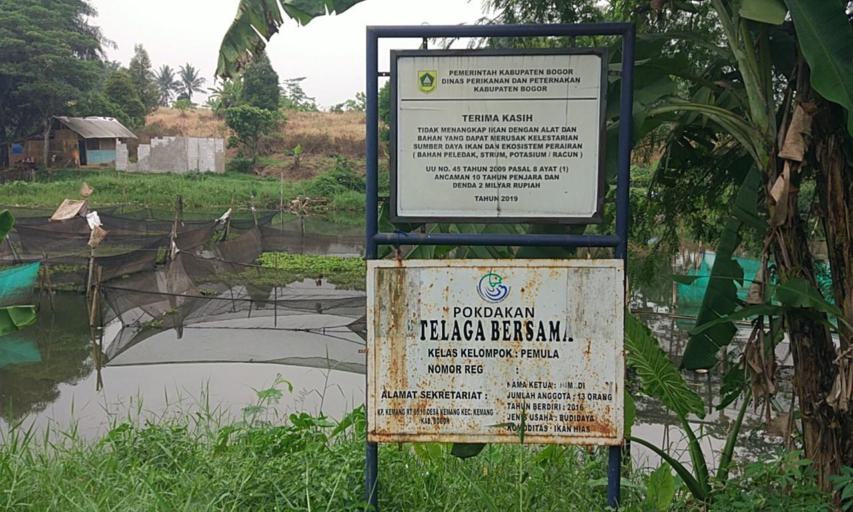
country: ID
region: West Java
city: Ciampea
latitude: -6.4967
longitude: 106.7477
